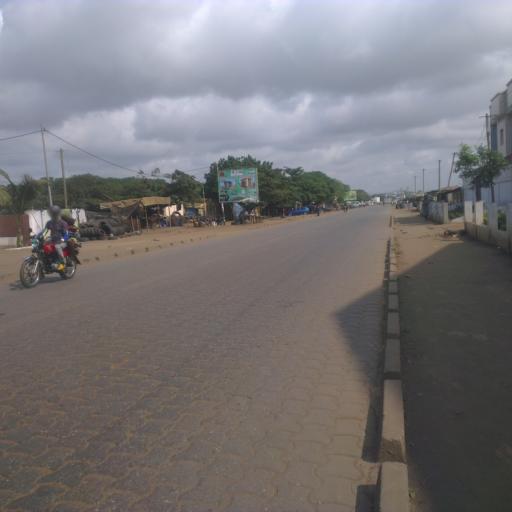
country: TG
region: Maritime
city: Lome
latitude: 6.1508
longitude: 1.2711
